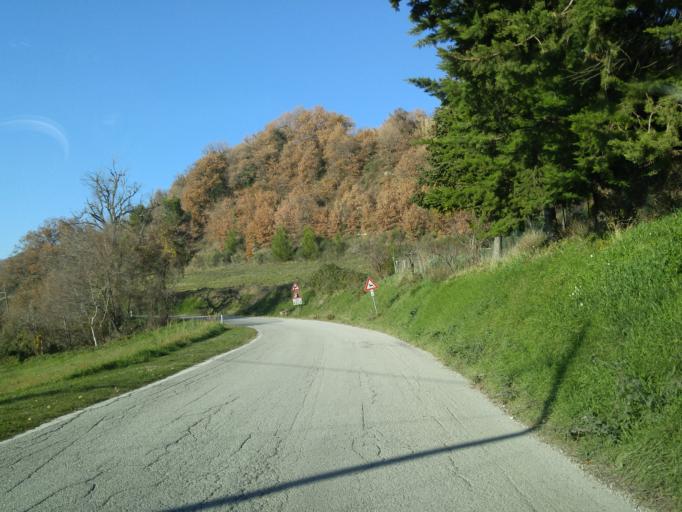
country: IT
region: The Marches
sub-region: Provincia di Pesaro e Urbino
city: Isola del Piano
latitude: 43.7665
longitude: 12.8013
